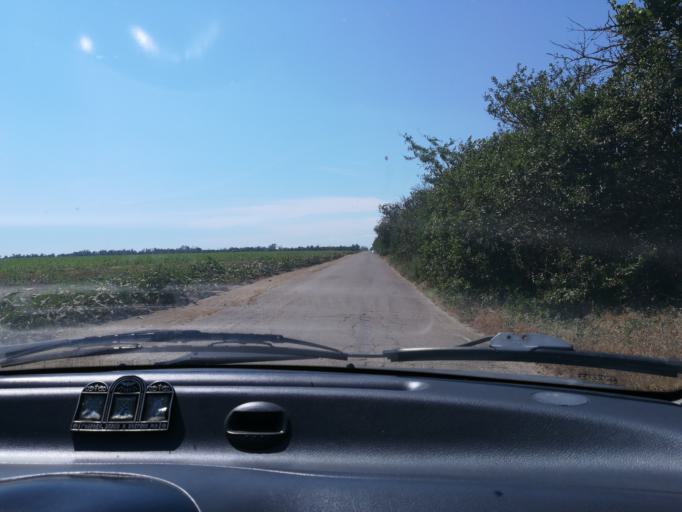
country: RU
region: Krasnodarskiy
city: Blagovetschenskaya
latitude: 45.0593
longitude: 37.0969
